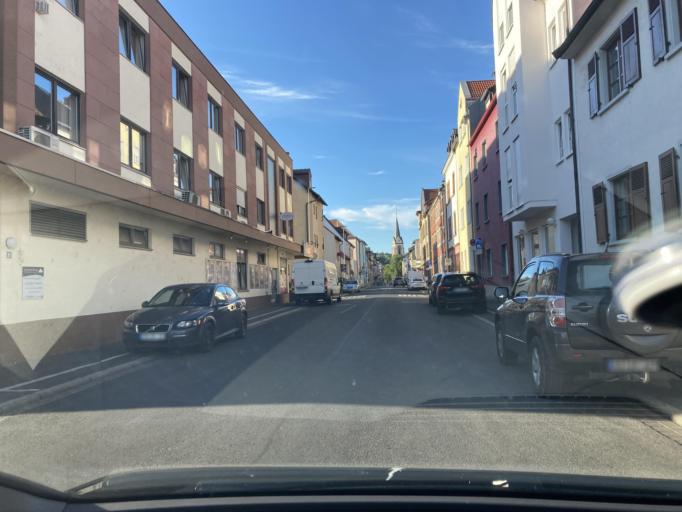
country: DE
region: Bavaria
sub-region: Regierungsbezirk Unterfranken
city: Aschaffenburg
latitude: 49.9825
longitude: 9.1354
